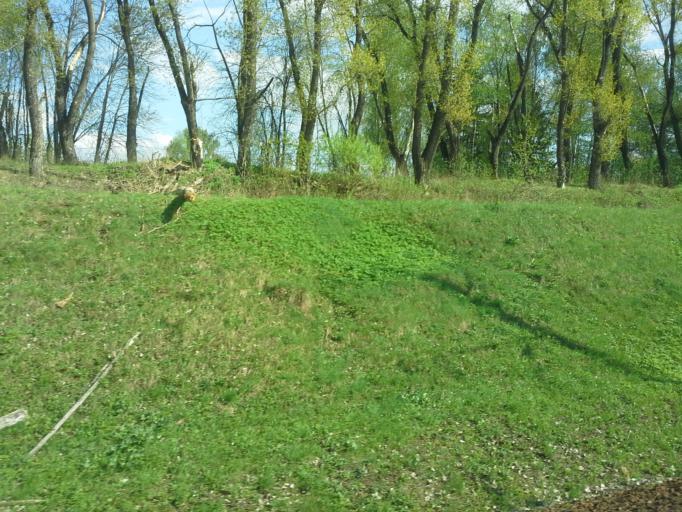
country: RU
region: Moskovskaya
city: Pushkino
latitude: 56.0326
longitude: 37.8504
